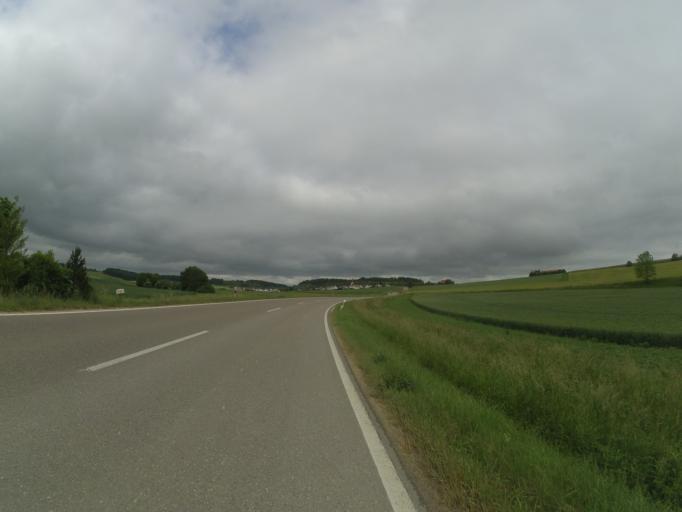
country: DE
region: Baden-Wuerttemberg
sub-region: Tuebingen Region
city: Bernstadt
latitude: 48.4821
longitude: 10.0417
